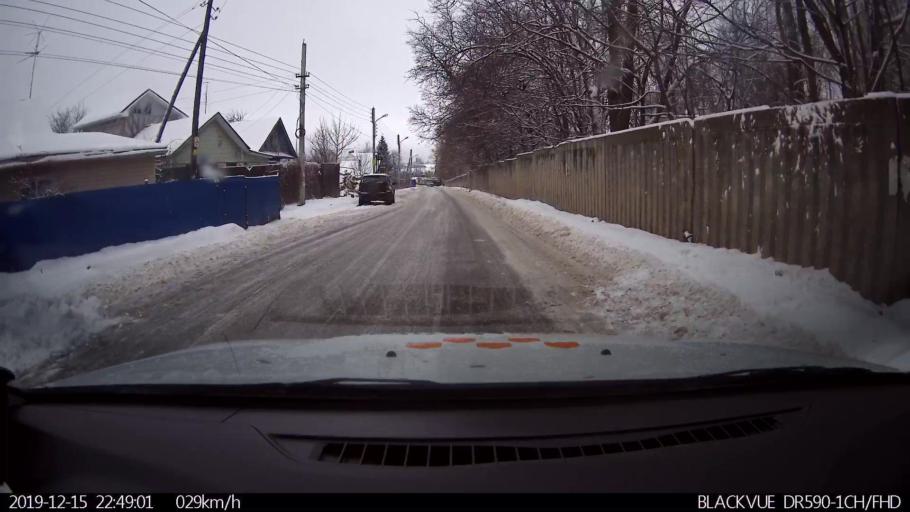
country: RU
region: Nizjnij Novgorod
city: Nizhniy Novgorod
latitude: 56.2357
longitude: 43.9776
